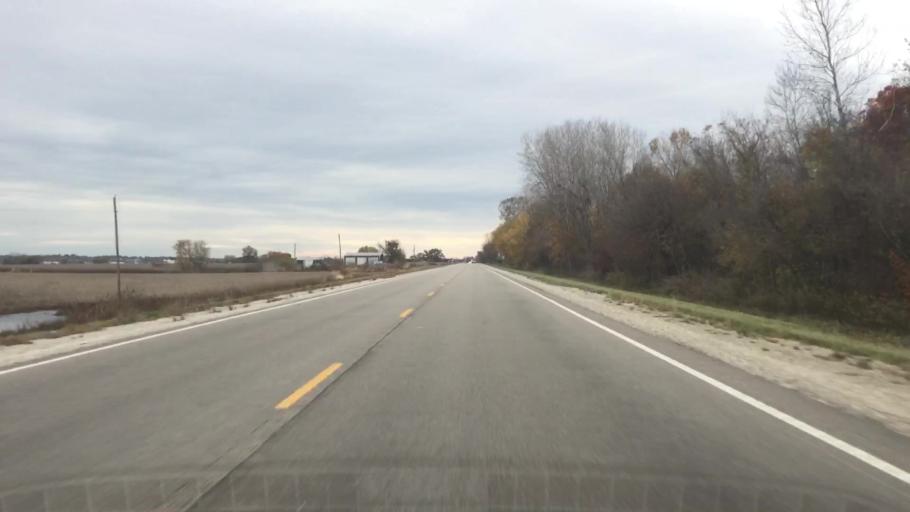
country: US
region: Missouri
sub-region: Cole County
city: Jefferson City
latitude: 38.5885
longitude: -92.1267
